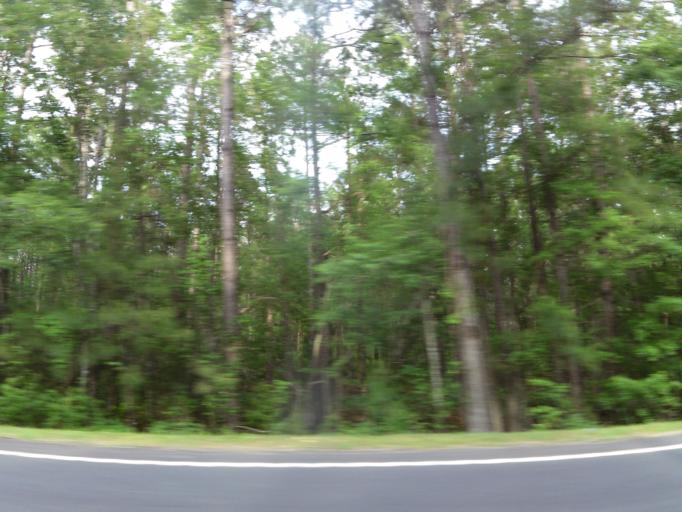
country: US
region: South Carolina
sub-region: Jasper County
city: Hardeeville
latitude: 32.3568
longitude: -81.0938
